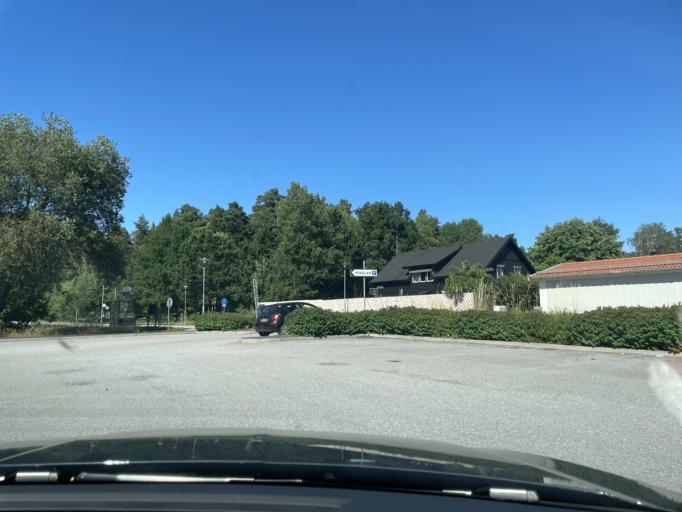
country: SE
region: Stockholm
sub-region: Sigtuna Kommun
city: Rosersberg
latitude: 59.5828
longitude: 17.8820
